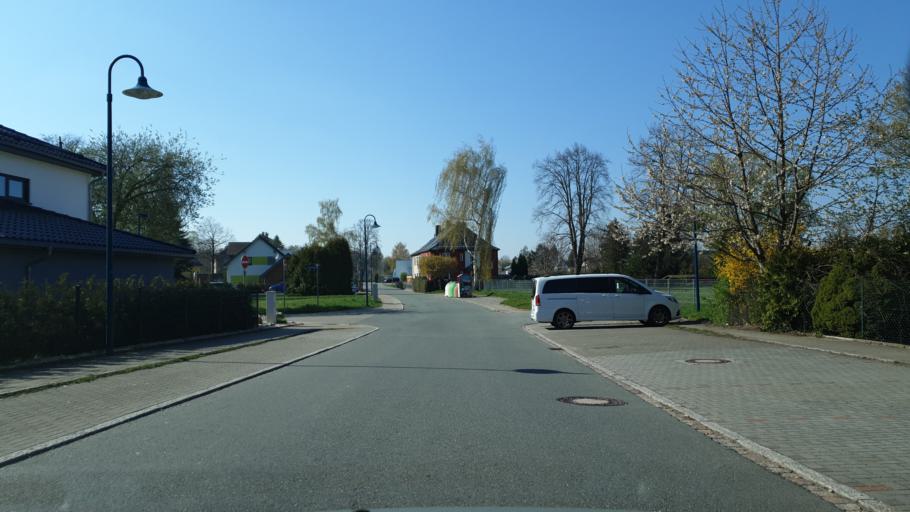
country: DE
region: Saxony
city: Oelsnitz
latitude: 50.7283
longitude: 12.7050
